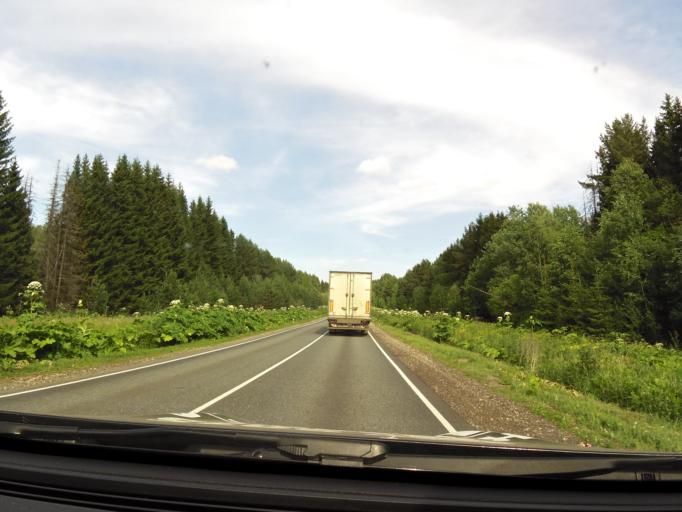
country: RU
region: Kirov
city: Slobodskoy
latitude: 58.7644
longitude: 50.3430
